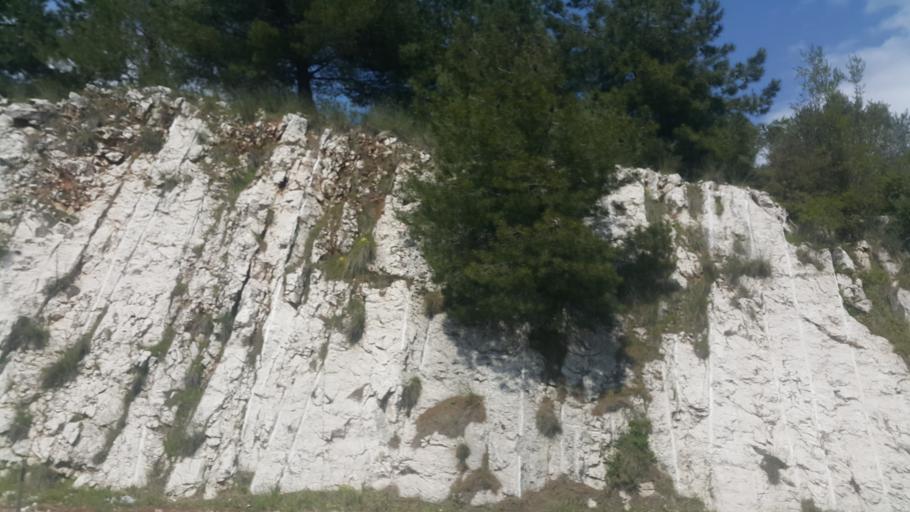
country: TR
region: Mersin
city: Camliyayla
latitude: 37.2036
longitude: 34.8166
